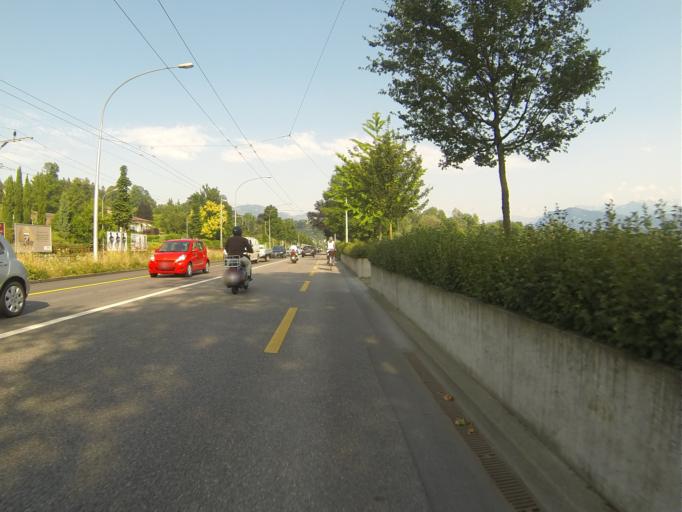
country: CH
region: Lucerne
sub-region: Lucerne-Stadt District
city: Luzern
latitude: 47.0550
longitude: 8.3302
